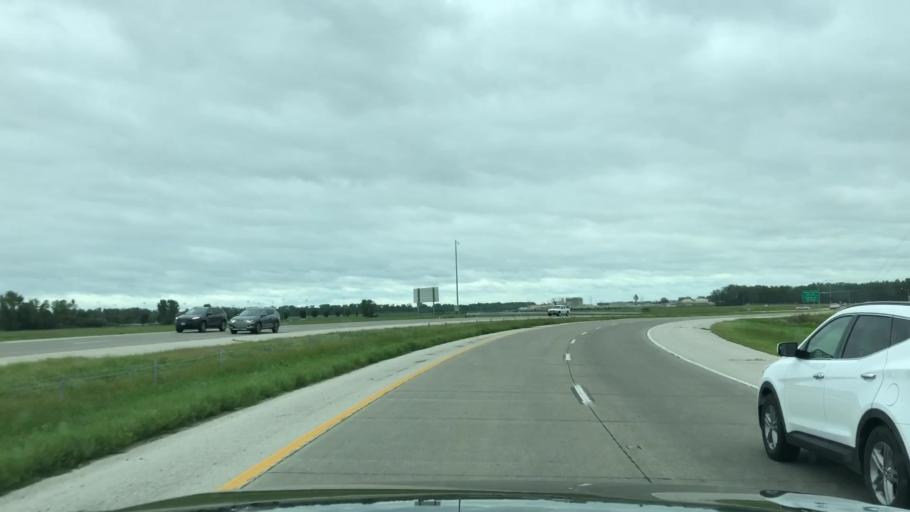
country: US
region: Missouri
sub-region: Saint Charles County
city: Saint Charles
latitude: 38.7261
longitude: -90.4984
